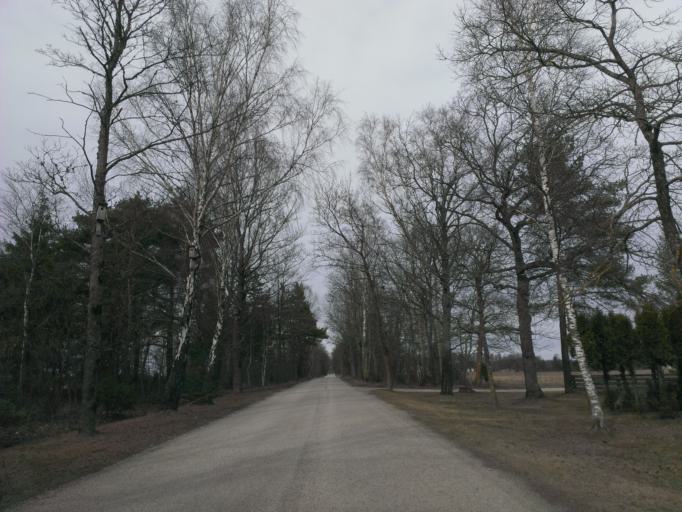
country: EE
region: Laeaene
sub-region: Lihula vald
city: Lihula
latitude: 58.5847
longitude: 23.5372
